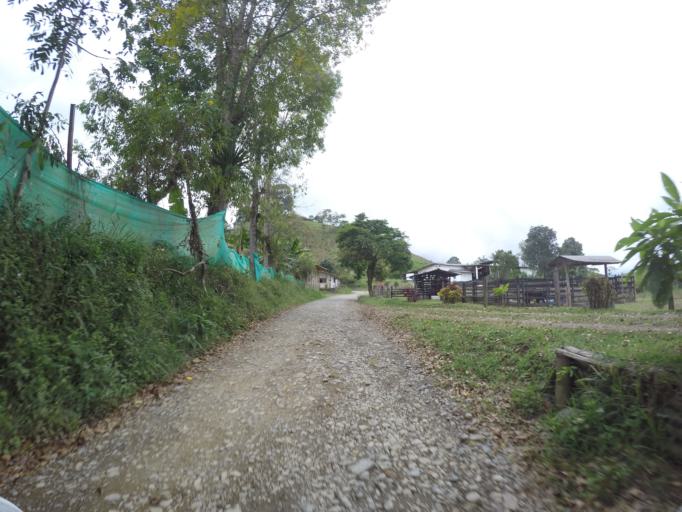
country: CO
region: Quindio
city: Filandia
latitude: 4.6493
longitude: -75.6739
